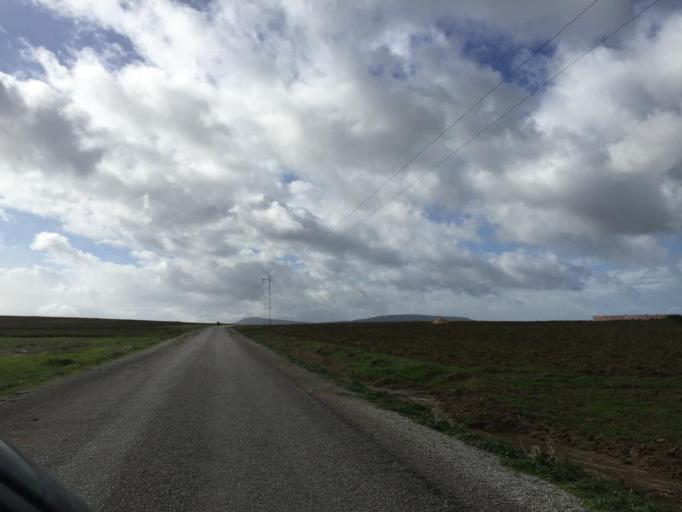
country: TN
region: Nabul
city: El Mida
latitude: 36.8888
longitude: 10.8621
